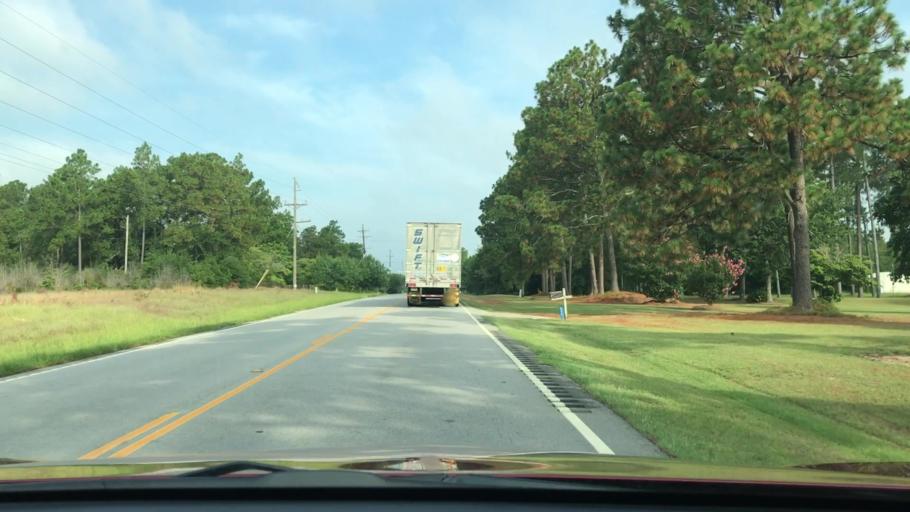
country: US
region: South Carolina
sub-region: Barnwell County
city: Williston
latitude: 33.6403
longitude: -81.3337
